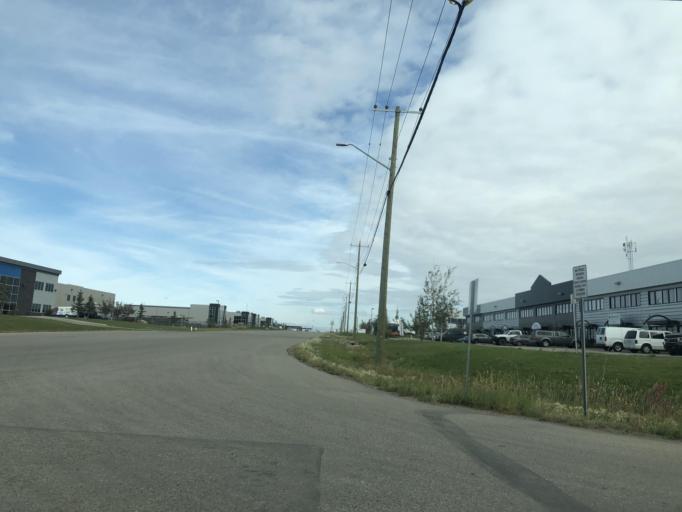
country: CA
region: Alberta
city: Chestermere
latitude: 50.9623
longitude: -113.9085
